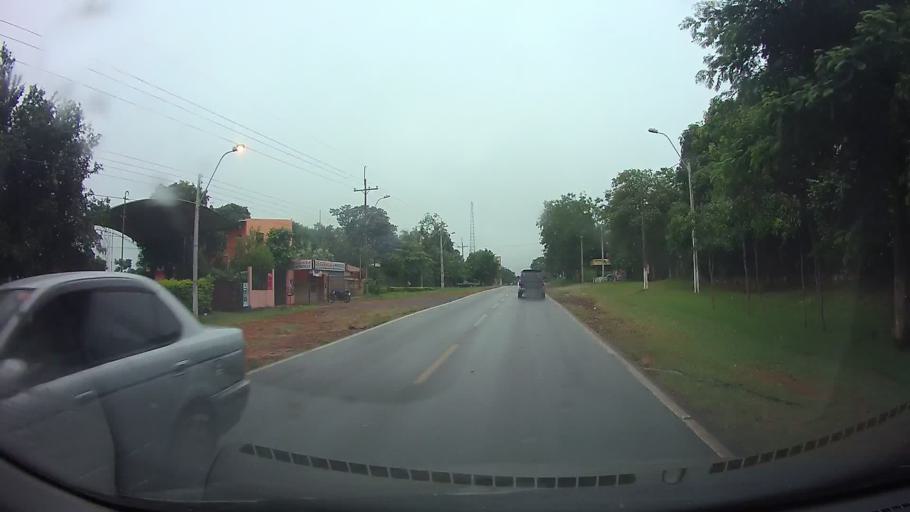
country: PY
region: Central
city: Ita
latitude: -25.4545
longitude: -57.3678
